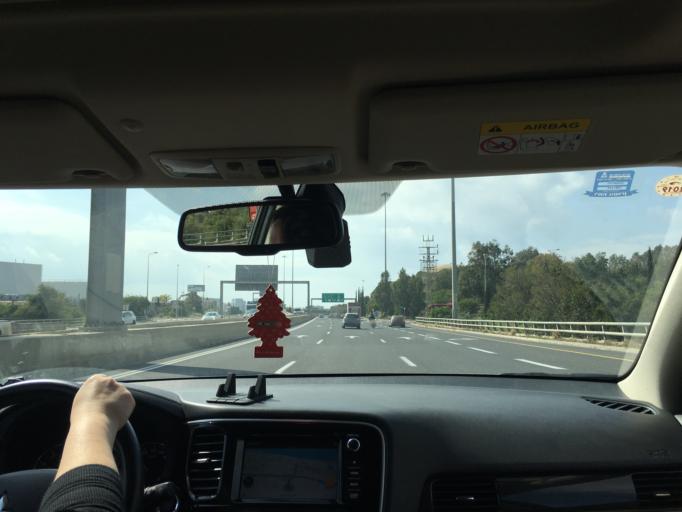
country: IL
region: Tel Aviv
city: Herzliyya
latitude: 32.1405
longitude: 34.8071
